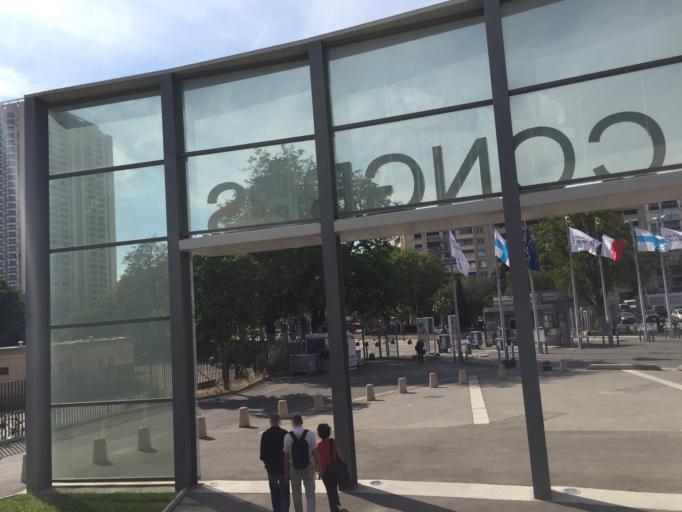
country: FR
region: Provence-Alpes-Cote d'Azur
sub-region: Departement des Bouches-du-Rhone
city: Marseille 08
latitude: 43.2720
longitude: 5.3933
